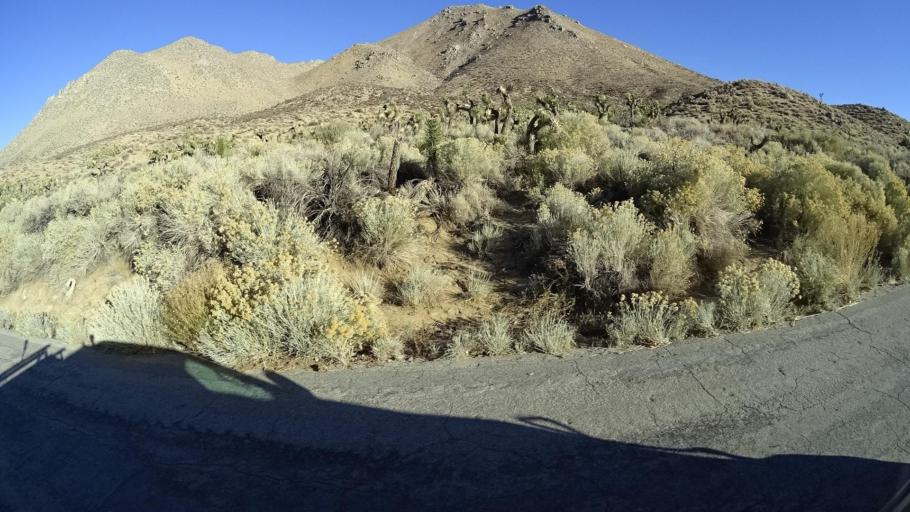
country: US
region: California
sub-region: Kern County
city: Weldon
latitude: 35.4663
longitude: -118.2114
